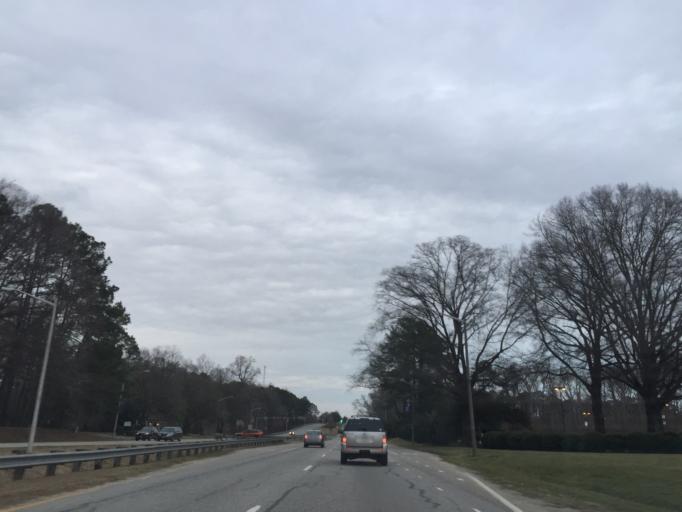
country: US
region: Virginia
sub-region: City of Newport News
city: Newport News
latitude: 37.0655
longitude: -76.4844
